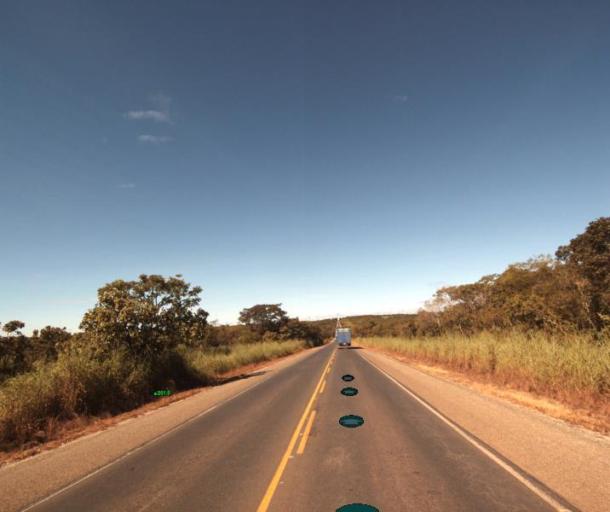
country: BR
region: Goias
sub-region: Itapaci
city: Itapaci
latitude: -14.9335
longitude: -49.3674
